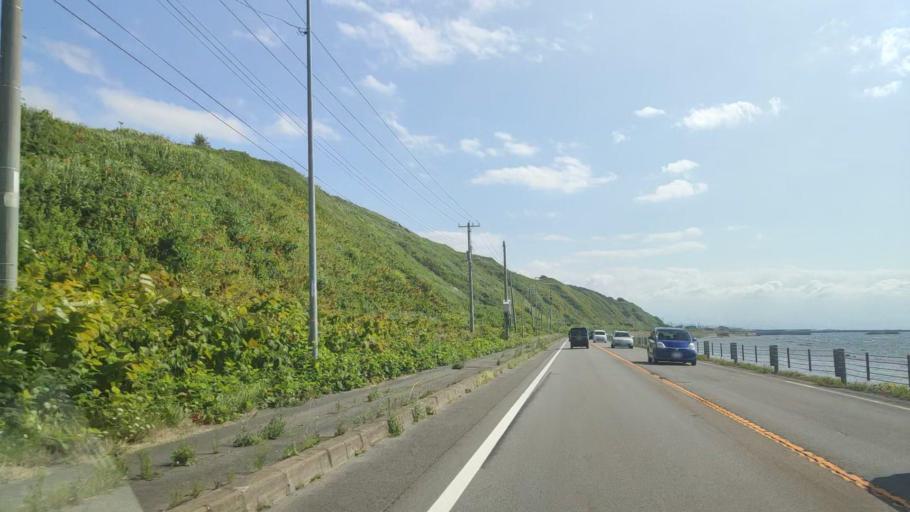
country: JP
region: Hokkaido
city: Rumoi
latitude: 43.9921
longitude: 141.6512
